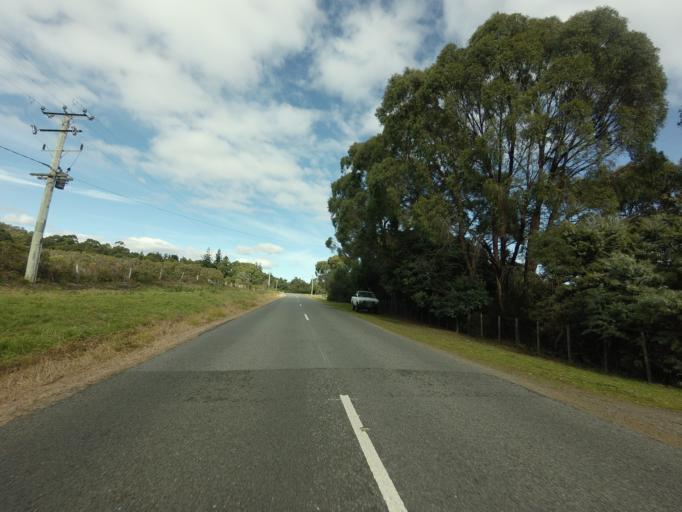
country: AU
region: Tasmania
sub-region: Clarence
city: Sandford
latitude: -43.0853
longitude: 147.7376
